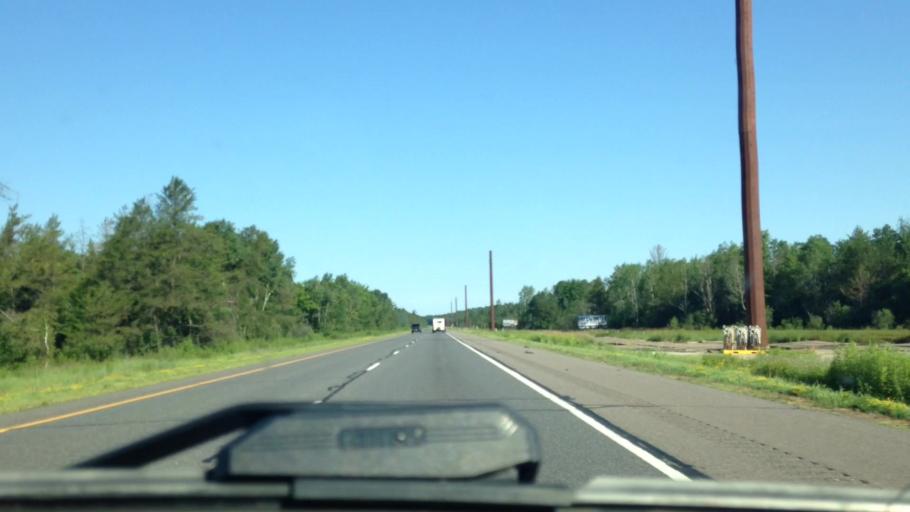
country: US
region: Wisconsin
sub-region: Jackson County
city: Black River Falls
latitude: 44.2576
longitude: -90.7624
